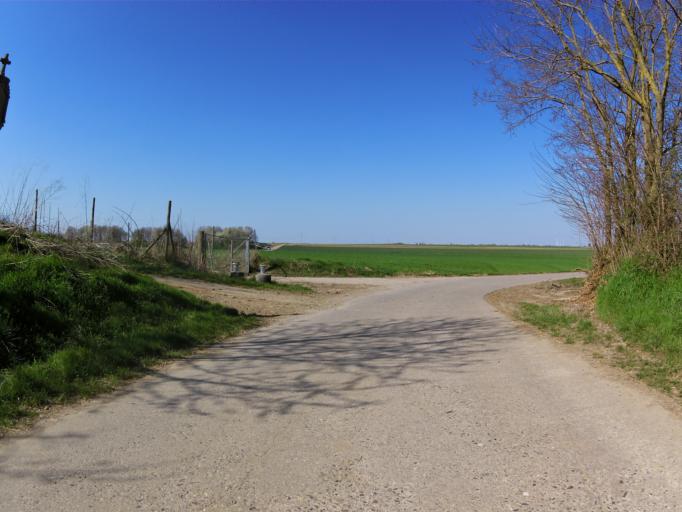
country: DE
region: Bavaria
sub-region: Regierungsbezirk Unterfranken
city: Oberpleichfeld
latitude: 49.8225
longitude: 10.0981
